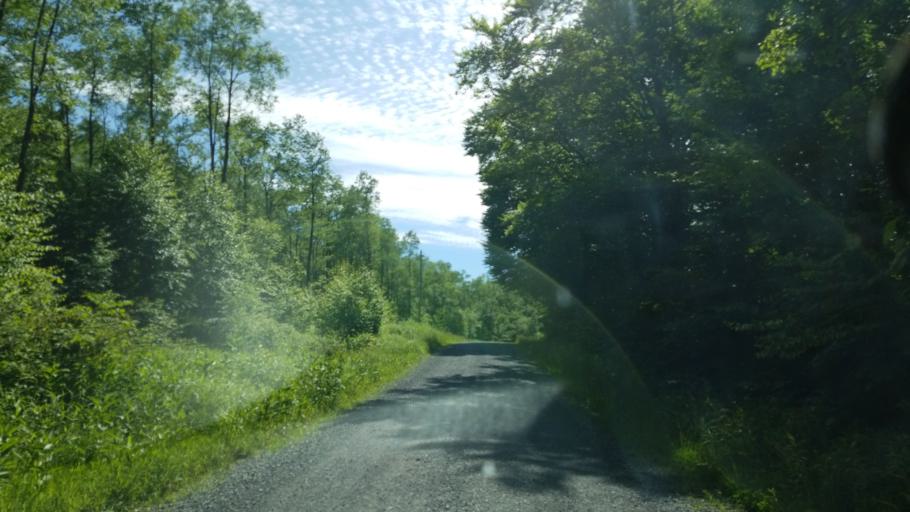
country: US
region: Pennsylvania
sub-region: Clearfield County
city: Clearfield
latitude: 41.1917
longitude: -78.4763
